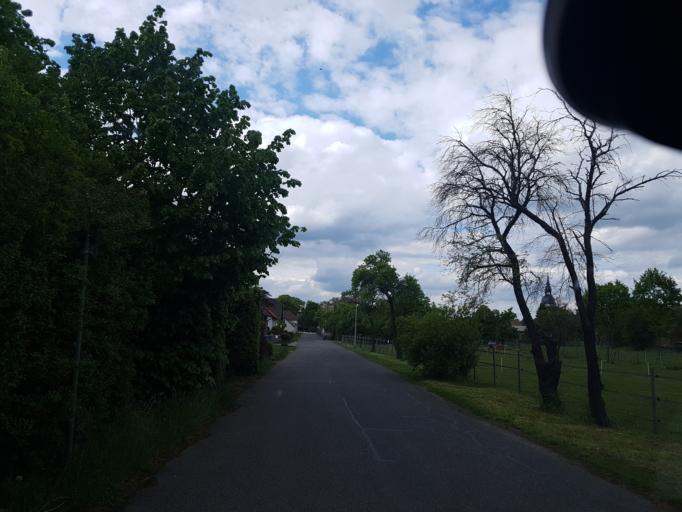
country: DE
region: Brandenburg
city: Grossraschen
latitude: 51.5857
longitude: 14.0621
